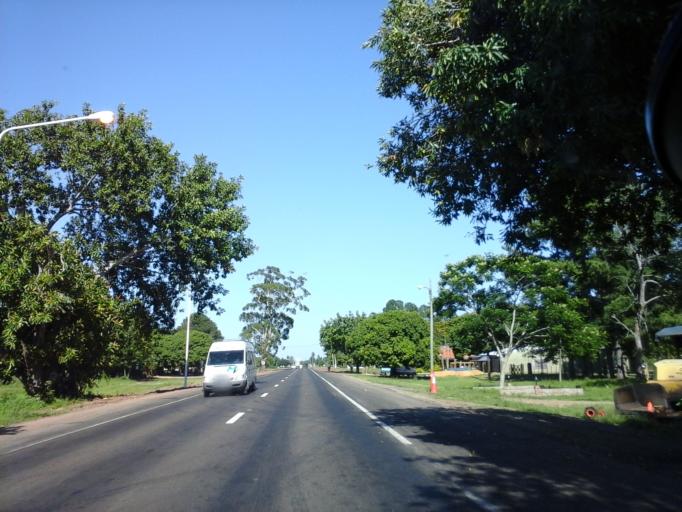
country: AR
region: Corrientes
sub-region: Departamento de Itati
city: Itati
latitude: -27.3670
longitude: -58.2904
